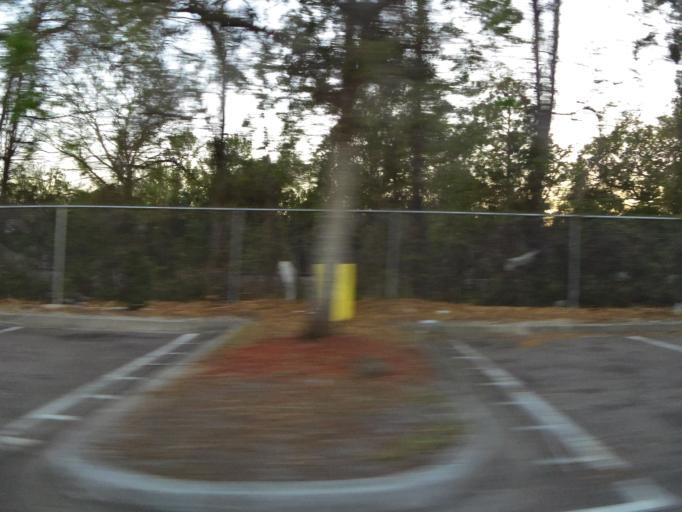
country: US
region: Florida
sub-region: Duval County
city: Jacksonville
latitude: 30.2805
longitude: -81.6310
